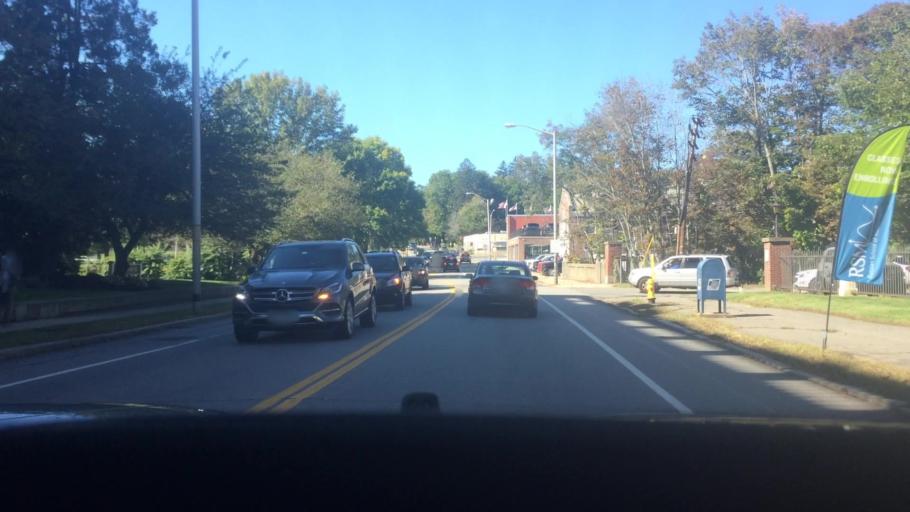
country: US
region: Massachusetts
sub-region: Essex County
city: Andover
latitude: 42.6726
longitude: -71.1488
